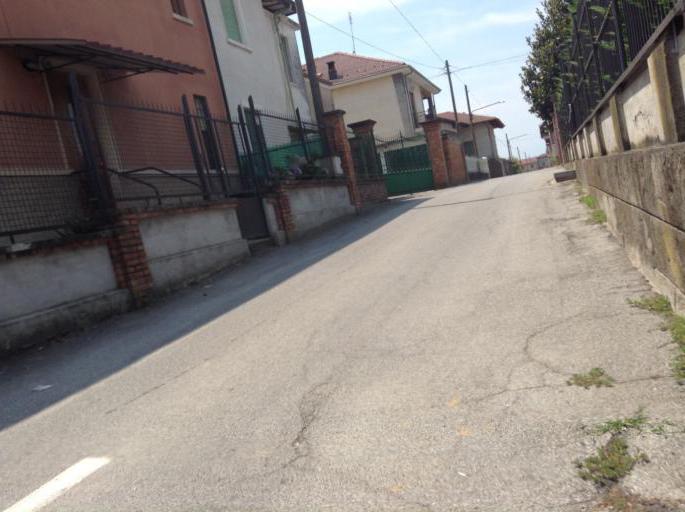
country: IT
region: Piedmont
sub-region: Provincia di Torino
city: Carignano
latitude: 44.8999
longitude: 7.6712
